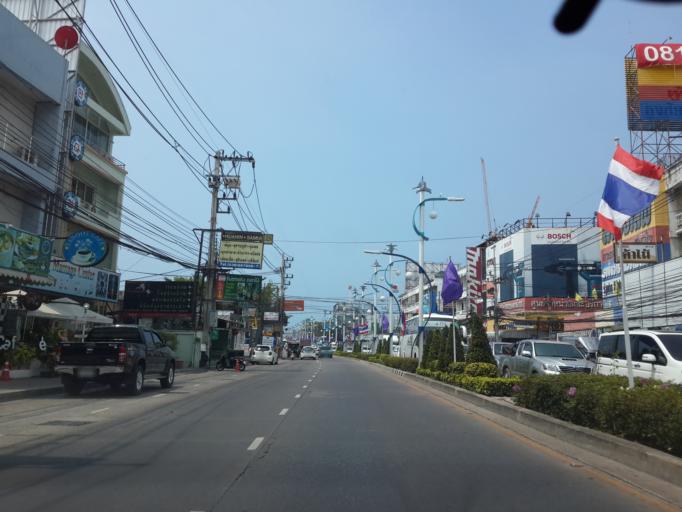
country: TH
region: Chon Buri
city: Phatthaya
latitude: 12.9488
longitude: 100.9046
